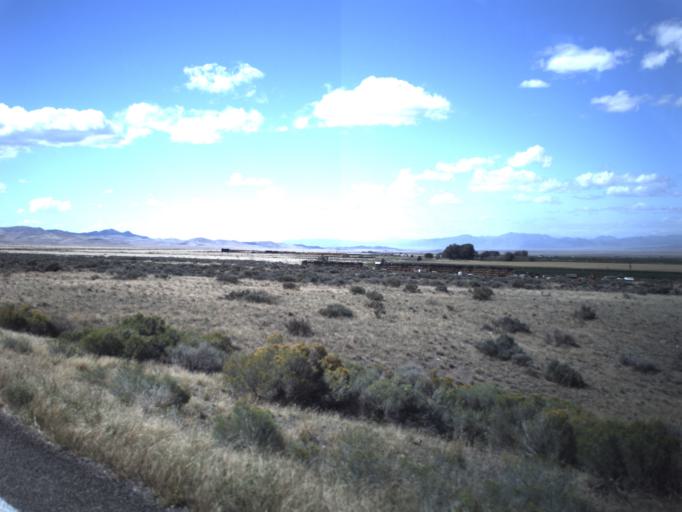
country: US
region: Utah
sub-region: Beaver County
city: Milford
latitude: 38.2048
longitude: -112.9277
